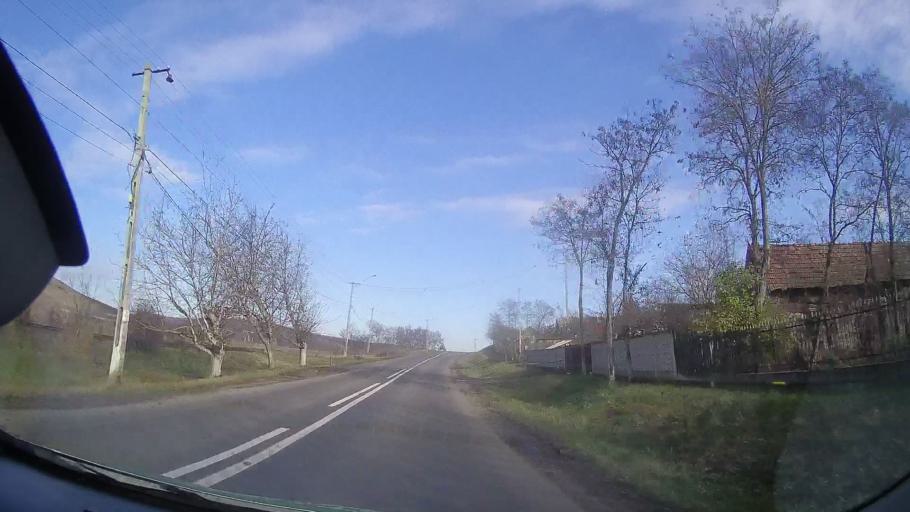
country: RO
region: Mures
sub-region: Comuna Valea Larga
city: Valea Larga
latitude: 46.5857
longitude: 24.0953
